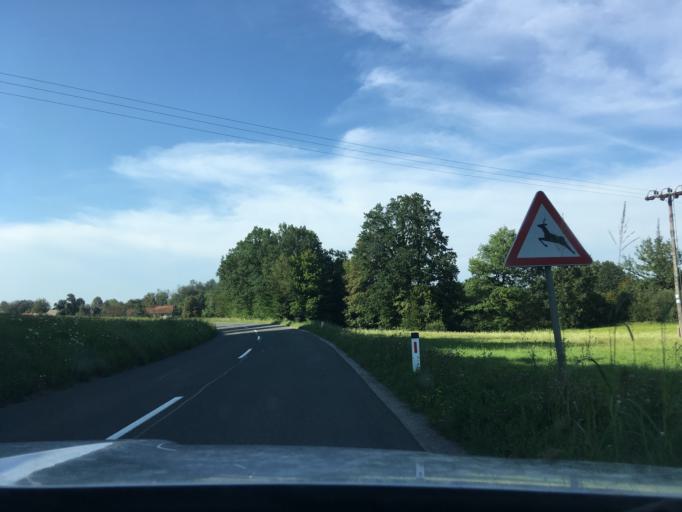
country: SI
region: Crnomelj
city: Crnomelj
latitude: 45.5041
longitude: 15.1899
